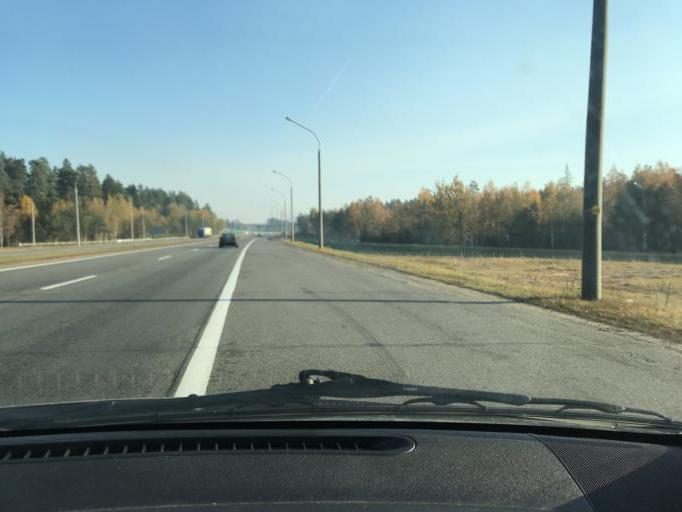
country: BY
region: Minsk
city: Slabada
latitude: 53.9496
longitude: 27.9788
